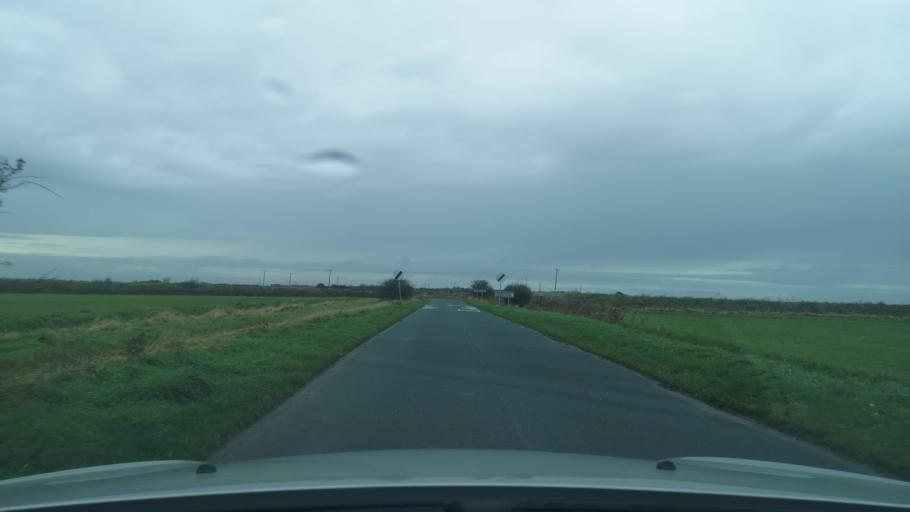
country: GB
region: England
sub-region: East Riding of Yorkshire
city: Easington
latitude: 53.6265
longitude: 0.1256
